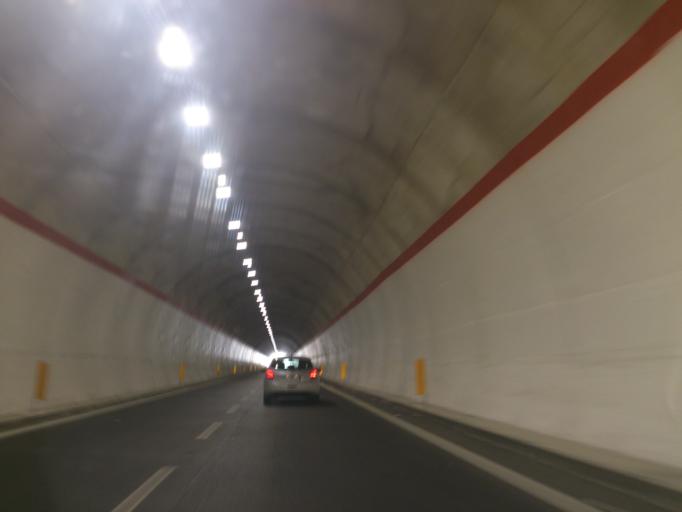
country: IT
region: Calabria
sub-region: Provincia di Reggio Calabria
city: Roccella Ionica
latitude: 38.3299
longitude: 16.4054
